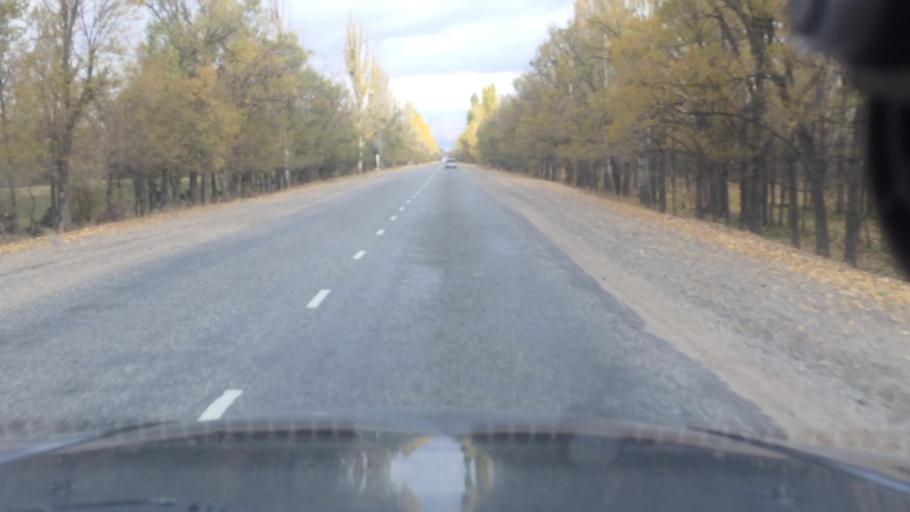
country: KG
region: Ysyk-Koel
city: Tyup
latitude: 42.6324
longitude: 78.3600
